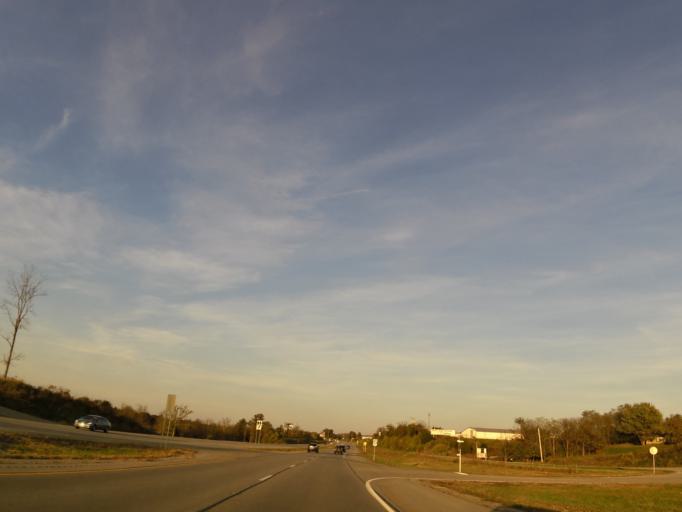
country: US
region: Kentucky
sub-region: Jessamine County
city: Wilmore
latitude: 37.7453
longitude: -84.6271
